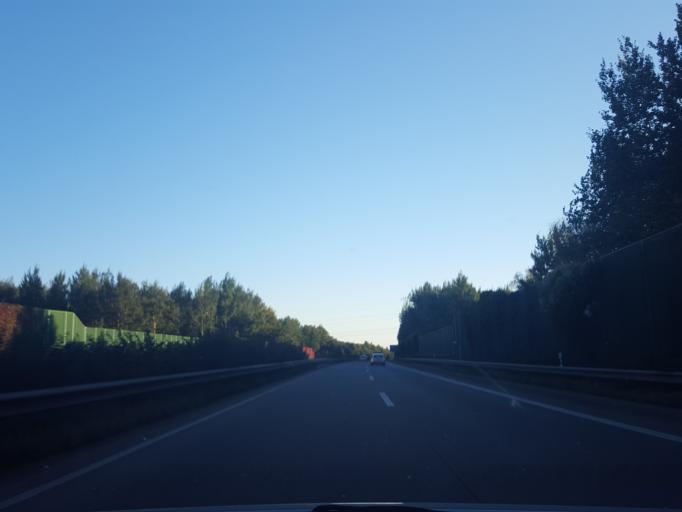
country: DE
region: Lower Saxony
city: Schiffdorf
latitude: 53.5105
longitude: 8.6289
